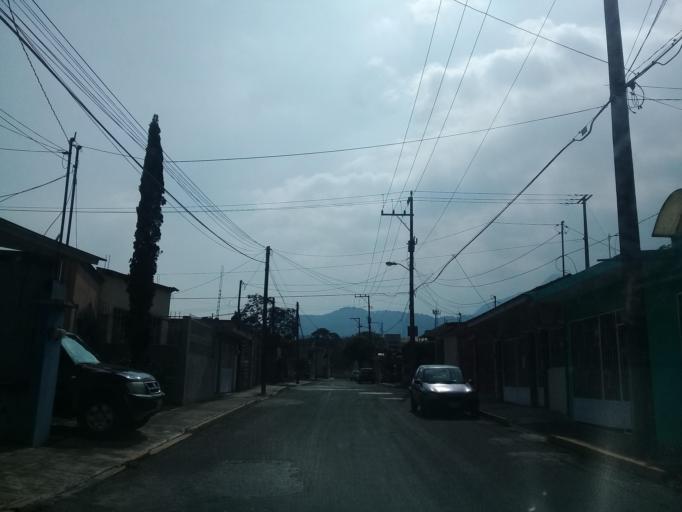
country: MX
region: Veracruz
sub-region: Mariano Escobedo
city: Palmira
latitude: 18.8748
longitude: -97.1012
